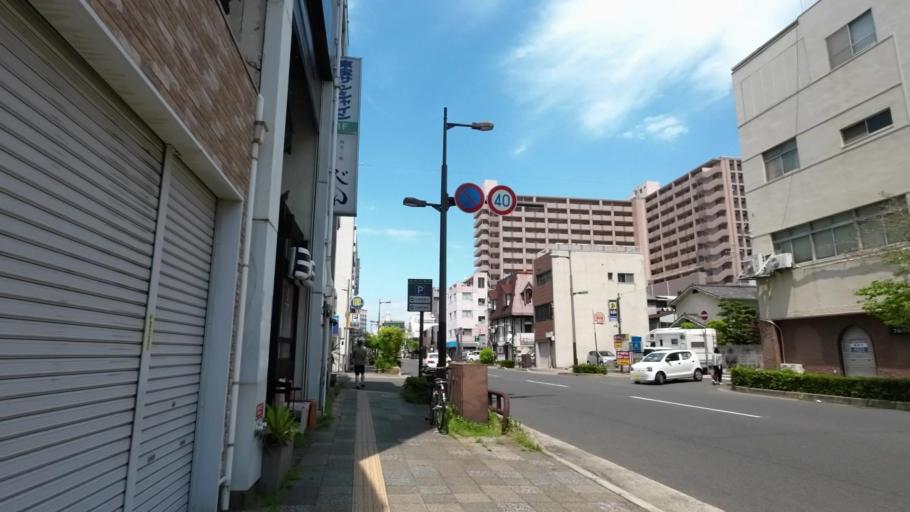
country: JP
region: Kagawa
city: Takamatsu-shi
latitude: 34.3443
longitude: 134.0528
